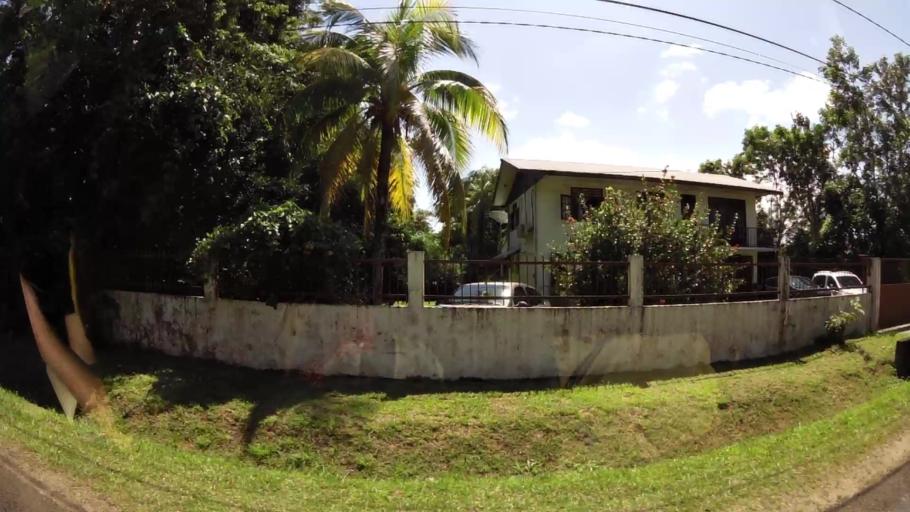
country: GF
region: Guyane
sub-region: Guyane
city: Matoury
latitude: 4.8400
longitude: -52.3274
